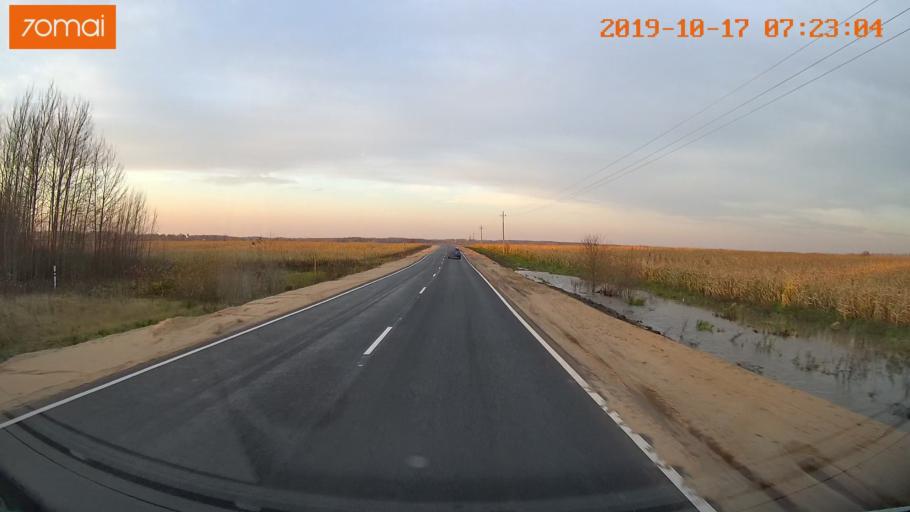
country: RU
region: Ivanovo
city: Gavrilov Posad
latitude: 56.3354
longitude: 40.1228
